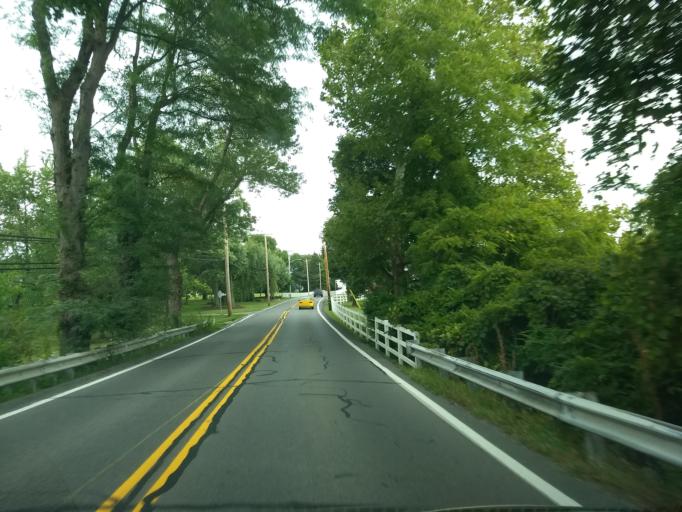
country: US
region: Pennsylvania
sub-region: Allegheny County
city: Carnot-Moon
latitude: 40.5034
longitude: -80.1988
